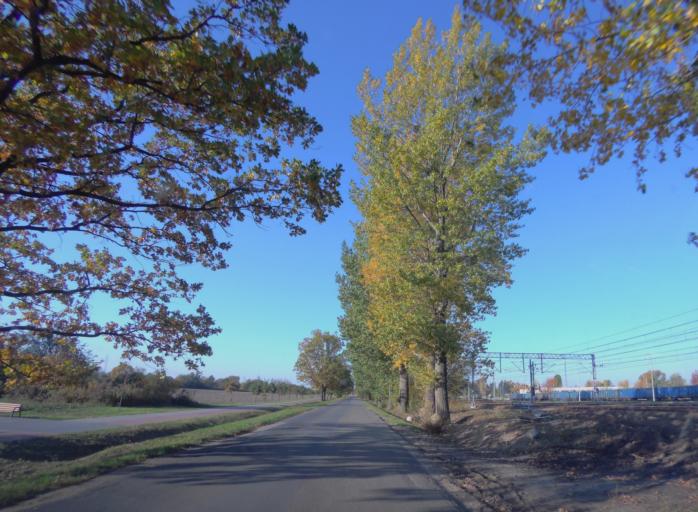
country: PL
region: Masovian Voivodeship
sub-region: Powiat pruszkowski
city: Otrebusy
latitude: 52.1603
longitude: 20.7755
